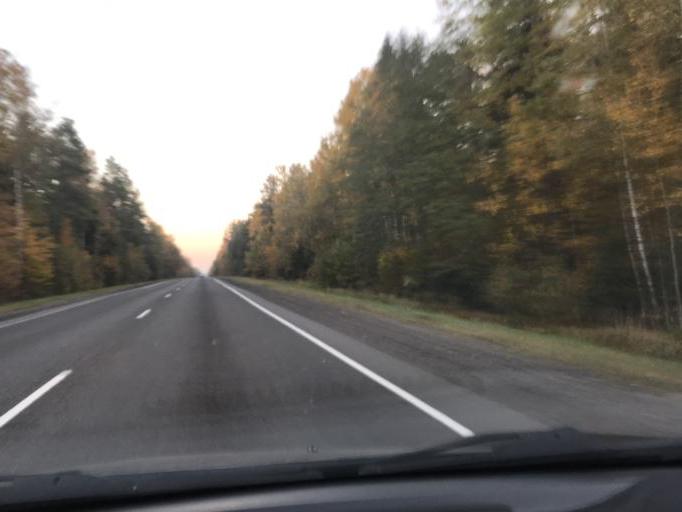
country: BY
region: Mogilev
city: Babruysk
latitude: 53.1355
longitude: 29.0502
